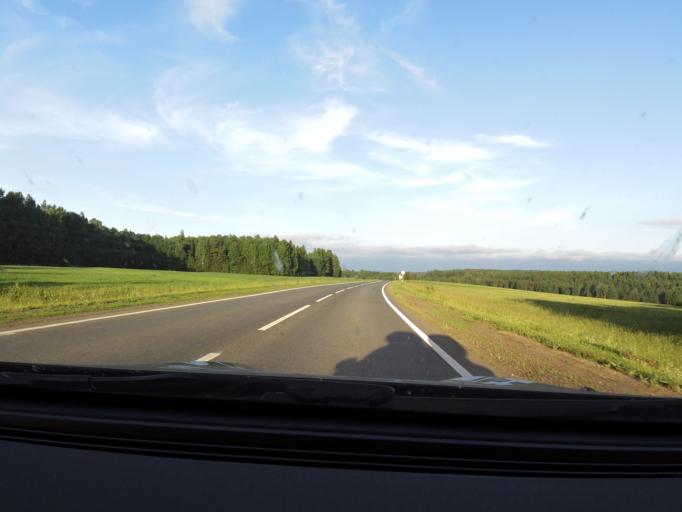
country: RU
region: Perm
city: Siva
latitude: 58.4887
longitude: 54.1256
